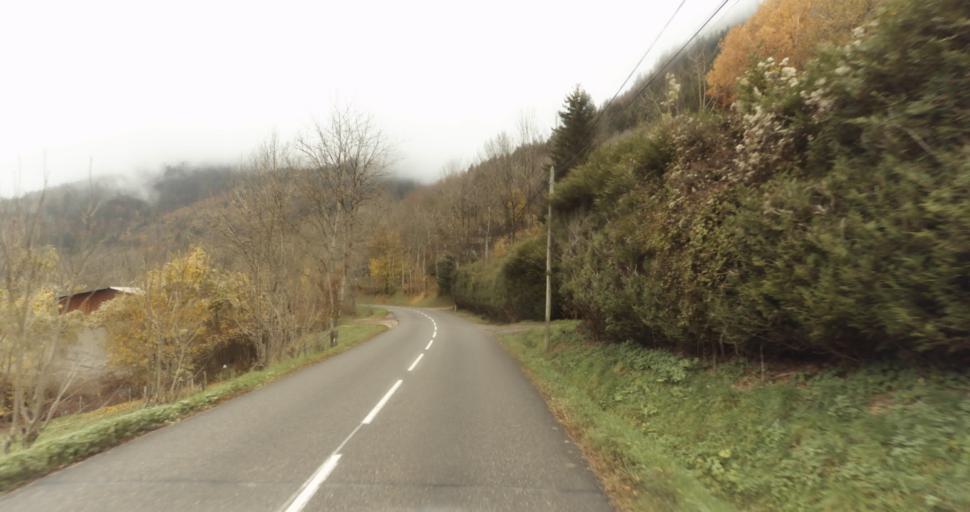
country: FR
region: Rhone-Alpes
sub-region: Departement de la Haute-Savoie
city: Thorens-Glieres
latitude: 45.9811
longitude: 6.2832
